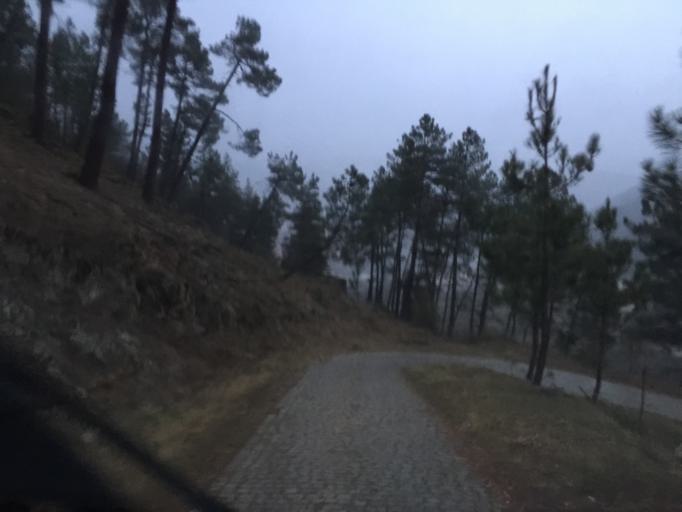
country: PT
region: Guarda
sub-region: Manteigas
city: Manteigas
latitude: 40.3859
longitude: -7.5460
